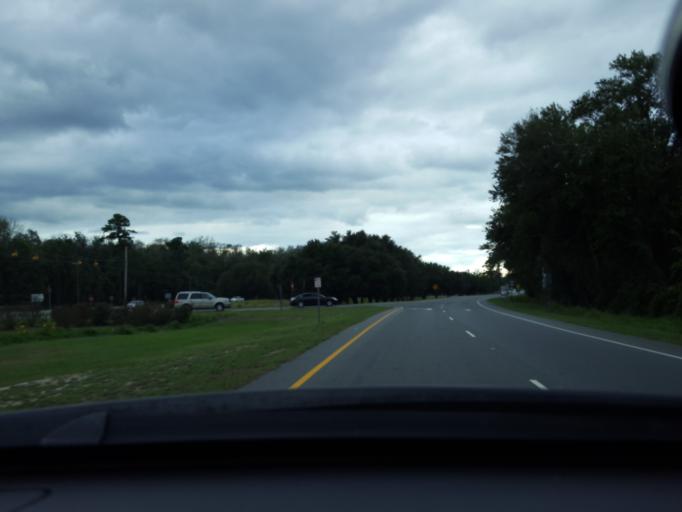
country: US
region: North Carolina
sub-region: Bladen County
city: Elizabethtown
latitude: 34.6498
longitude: -78.5228
